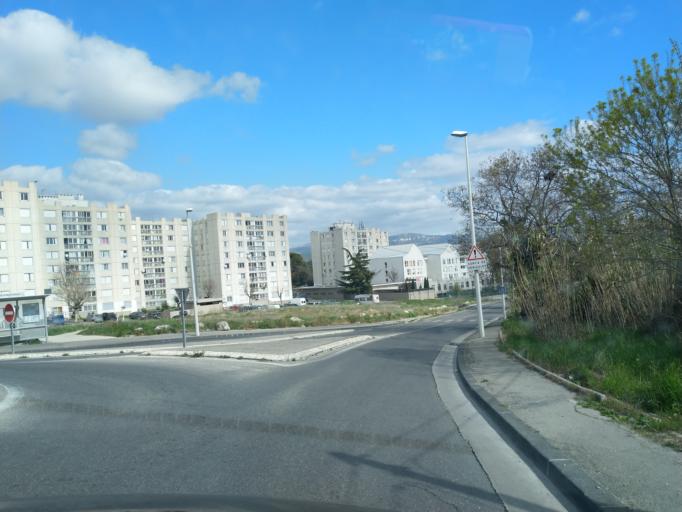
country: FR
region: Provence-Alpes-Cote d'Azur
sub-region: Departement des Bouches-du-Rhone
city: Plan-de-Cuques
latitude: 43.3278
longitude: 5.4544
